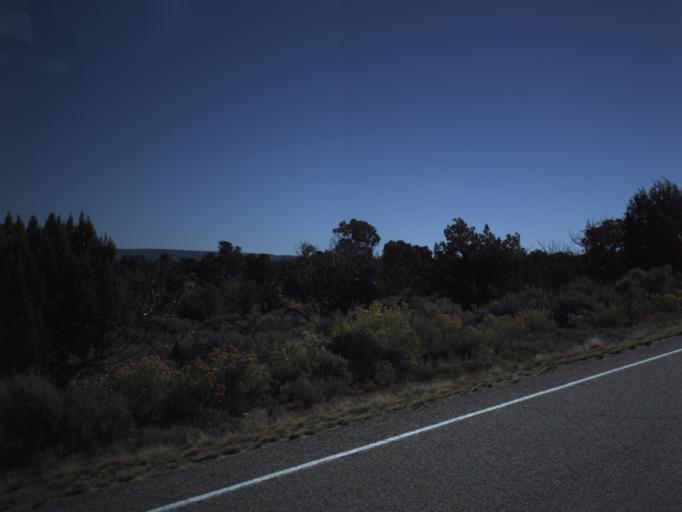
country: US
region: Utah
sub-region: San Juan County
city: Blanding
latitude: 37.5662
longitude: -110.0308
